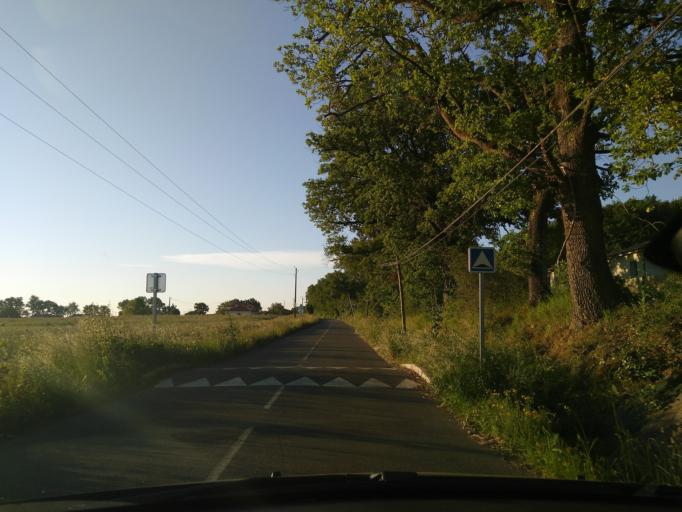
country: FR
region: Midi-Pyrenees
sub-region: Departement de la Haute-Garonne
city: Merville
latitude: 43.7290
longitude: 1.2947
